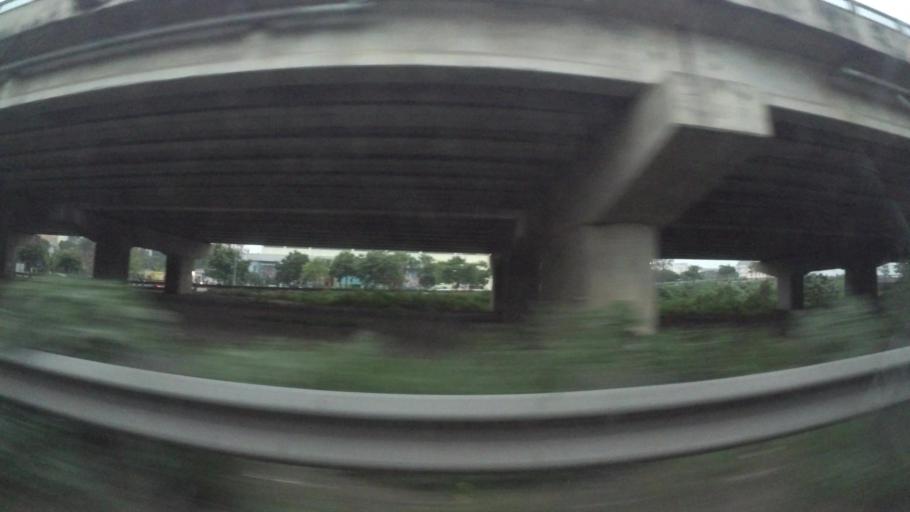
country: VN
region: Ha Noi
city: Van Dien
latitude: 20.9655
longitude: 105.8462
